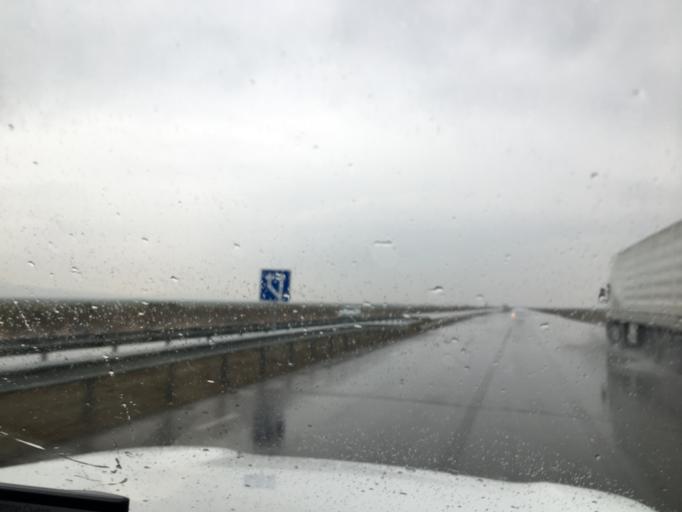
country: TM
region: Ahal
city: Annau
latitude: 37.8046
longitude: 58.7932
